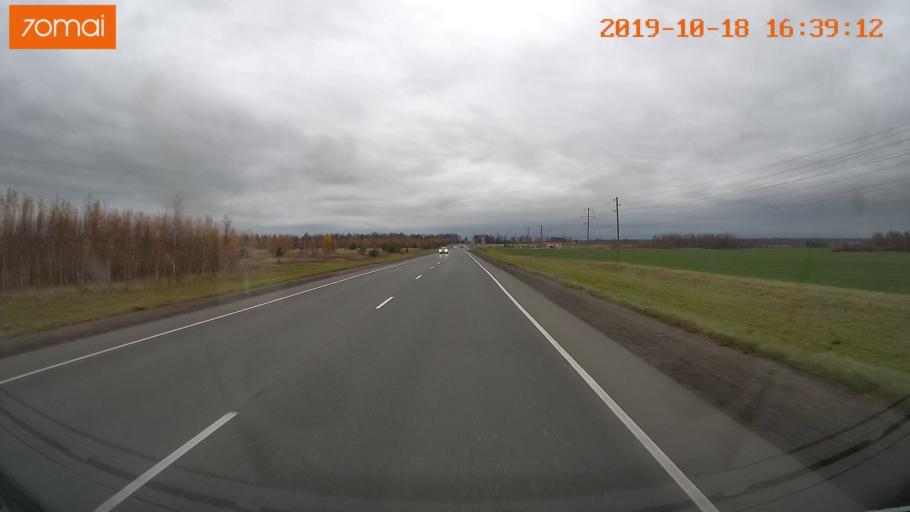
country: RU
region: Vladimir
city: Suzdal'
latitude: 56.4476
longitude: 40.4630
